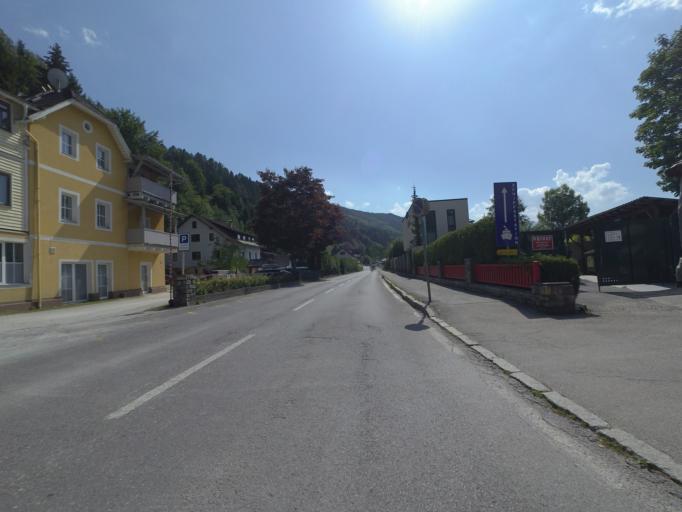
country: AT
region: Carinthia
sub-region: Politischer Bezirk Villach Land
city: Ferndorf
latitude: 46.7677
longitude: 13.6486
